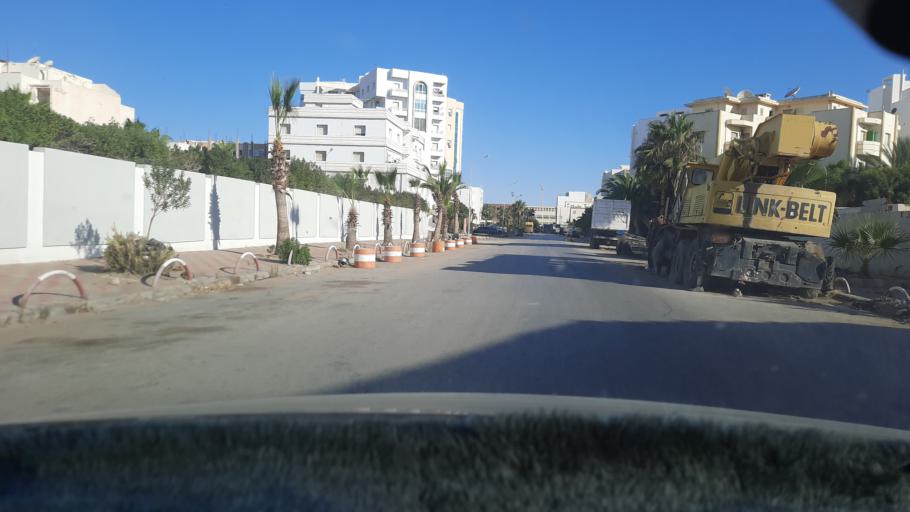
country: TN
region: Safaqis
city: Sfax
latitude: 34.7292
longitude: 10.7523
